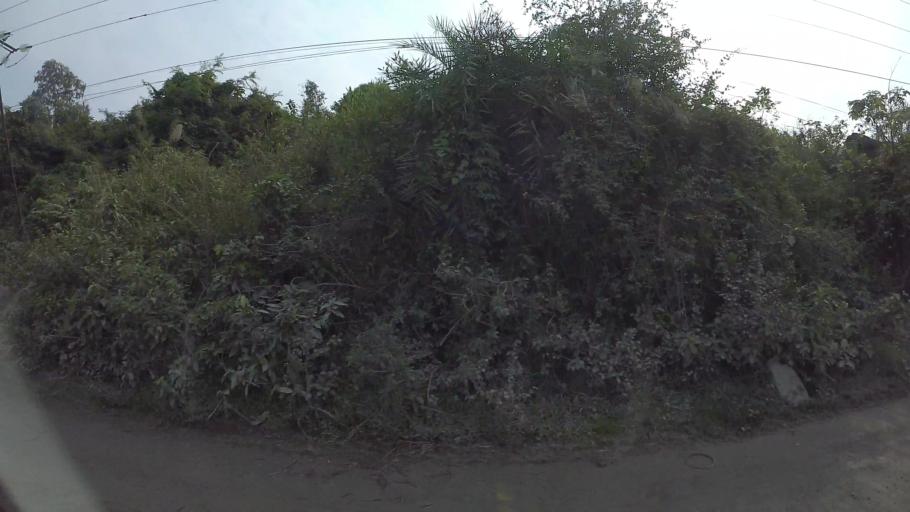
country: VN
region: Da Nang
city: Lien Chieu
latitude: 16.0407
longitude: 108.1509
